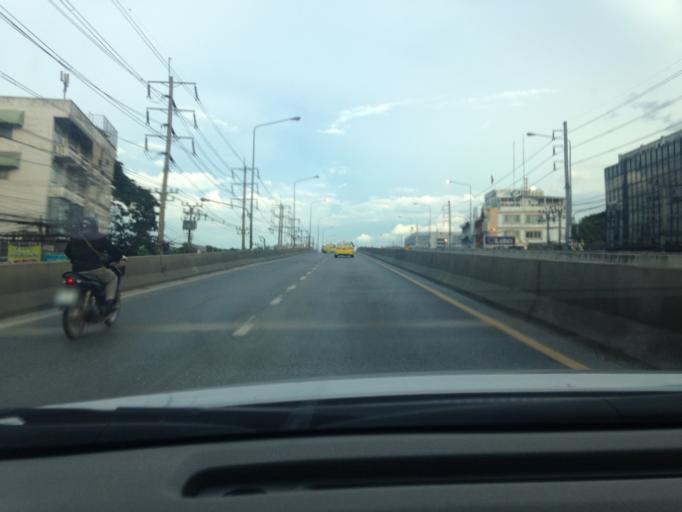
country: TH
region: Bangkok
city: Lak Si
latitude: 13.8925
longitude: 100.5624
